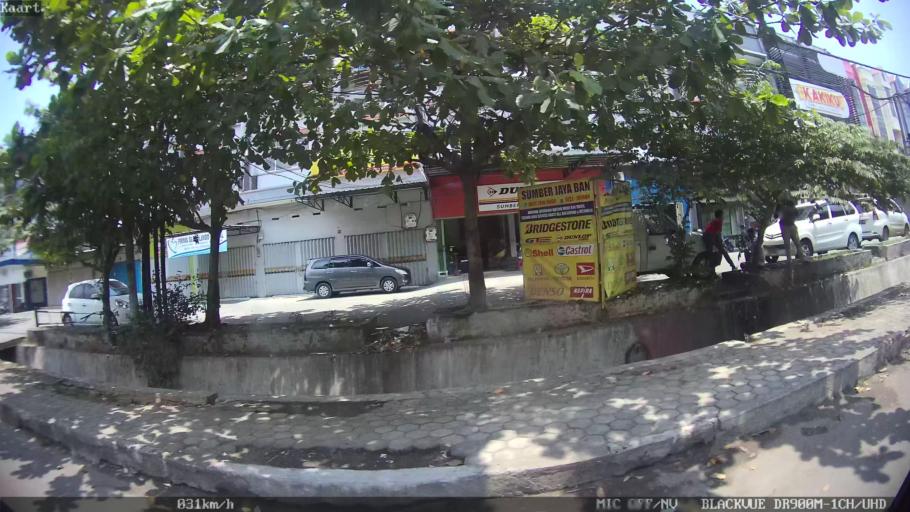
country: ID
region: Lampung
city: Kedaton
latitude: -5.3829
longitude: 105.2789
